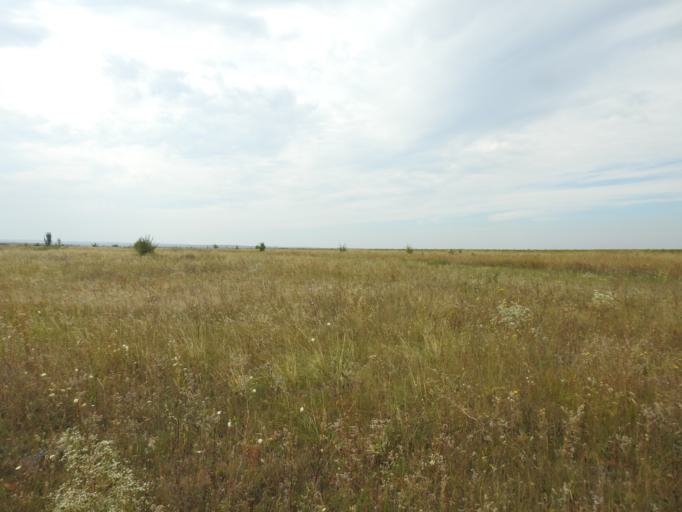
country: RU
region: Volgograd
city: Zhirnovsk
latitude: 51.2071
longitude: 44.9297
